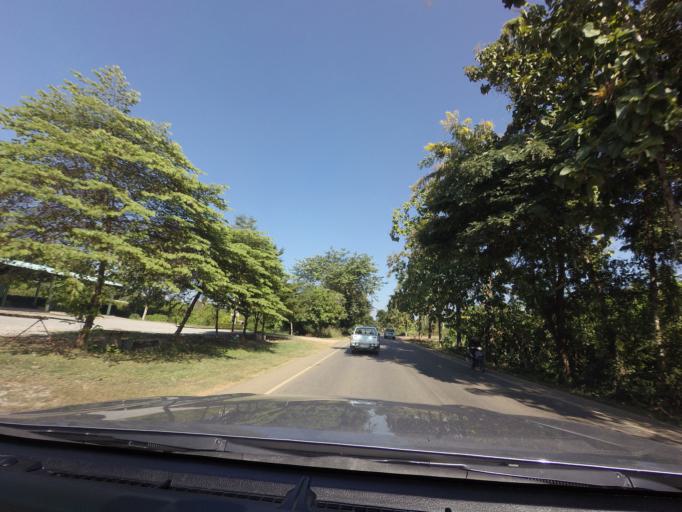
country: TH
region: Sukhothai
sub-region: Amphoe Si Satchanalai
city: Si Satchanalai
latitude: 17.6741
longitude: 99.6963
